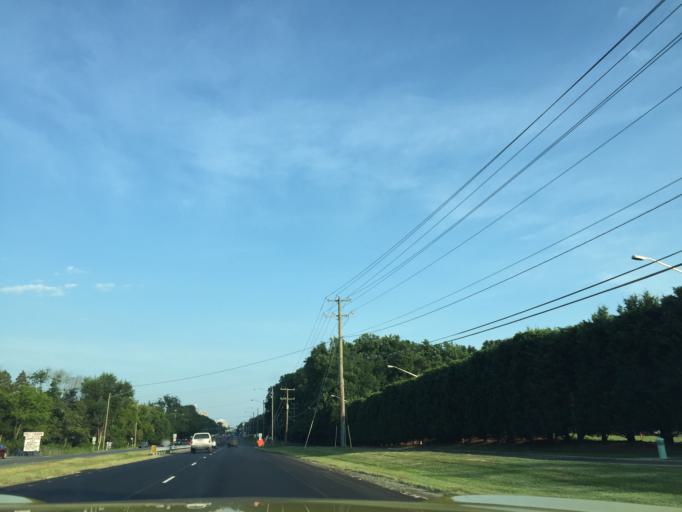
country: US
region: Virginia
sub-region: Fairfax County
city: Wolf Trap
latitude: 38.9470
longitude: -77.2595
